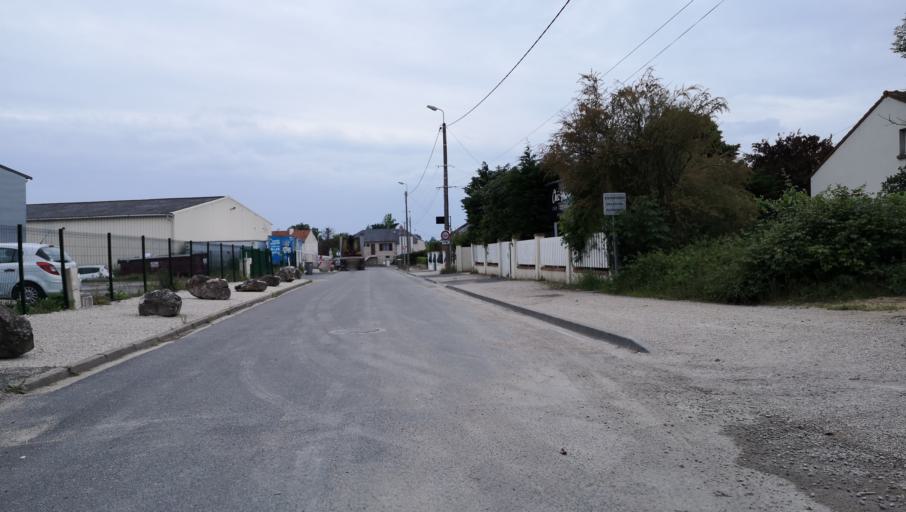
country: FR
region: Centre
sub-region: Departement du Loiret
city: Fleury-les-Aubrais
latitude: 47.9474
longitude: 1.9116
